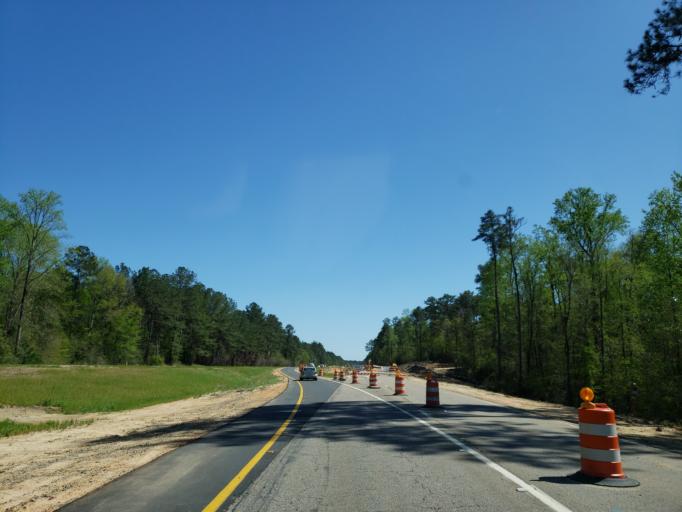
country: US
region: Mississippi
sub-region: Lamar County
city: Purvis
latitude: 31.1207
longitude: -89.2238
